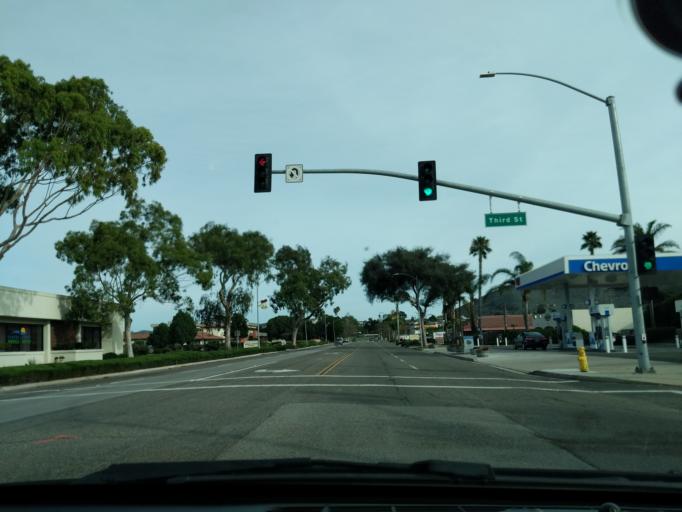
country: US
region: California
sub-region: Santa Barbara County
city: Lompoc
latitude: 34.6389
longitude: -120.4453
